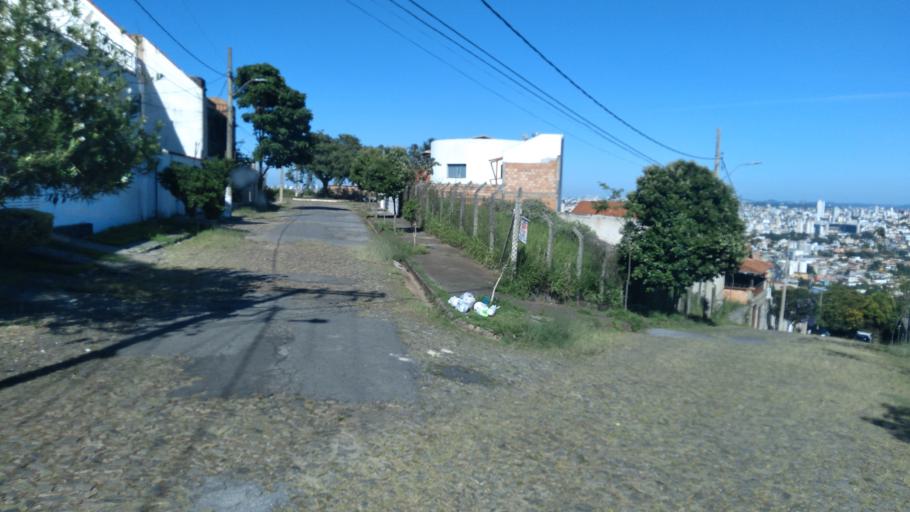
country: BR
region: Minas Gerais
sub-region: Belo Horizonte
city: Belo Horizonte
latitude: -19.9212
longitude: -43.8942
